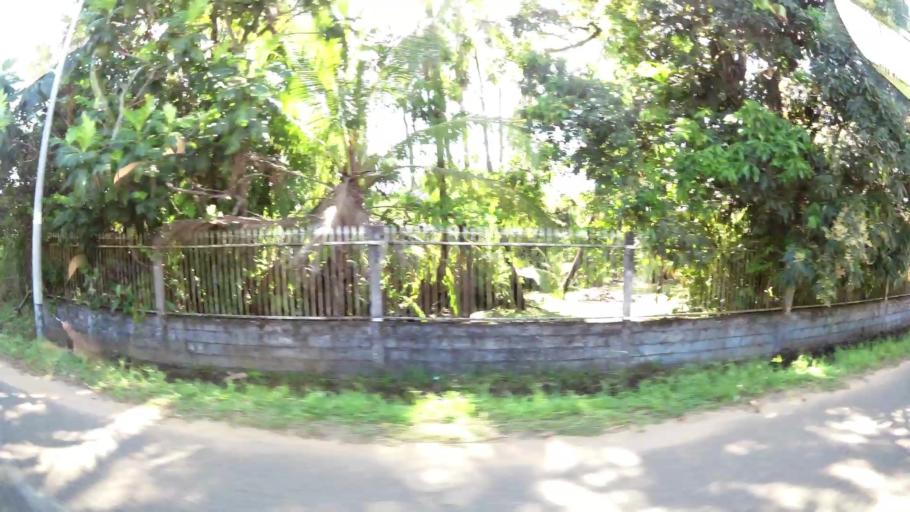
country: GF
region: Guyane
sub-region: Guyane
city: Remire-Montjoly
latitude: 4.9063
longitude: -52.2731
